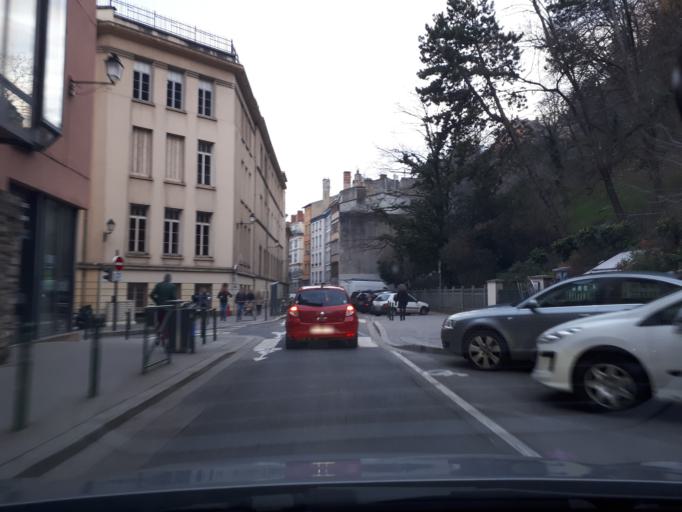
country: FR
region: Rhone-Alpes
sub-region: Departement du Rhone
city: Lyon
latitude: 45.7612
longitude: 4.8259
